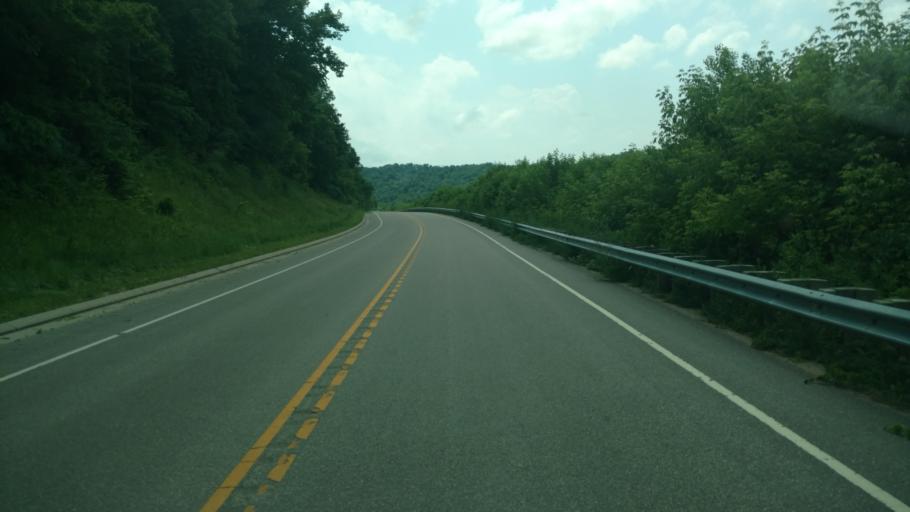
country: US
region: Wisconsin
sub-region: Vernon County
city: Viroqua
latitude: 43.4604
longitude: -90.7509
